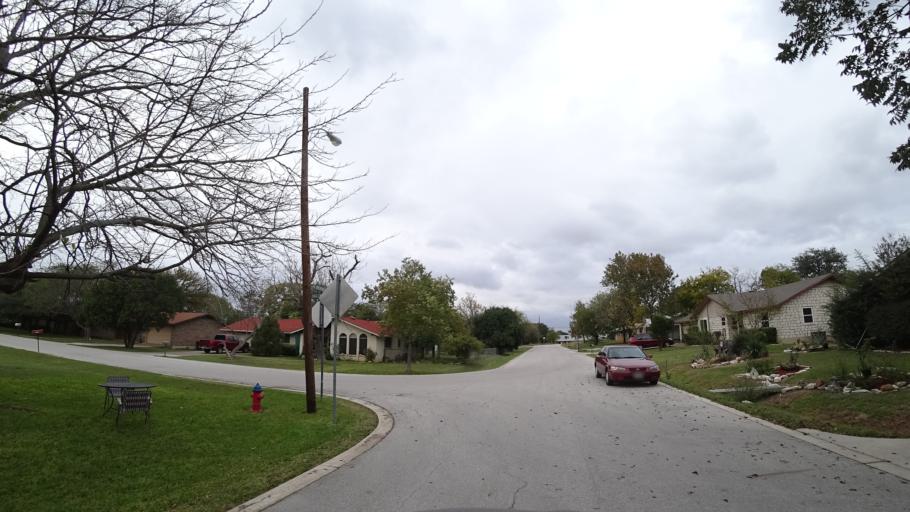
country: US
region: Texas
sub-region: Williamson County
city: Round Rock
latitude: 30.5101
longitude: -97.6916
